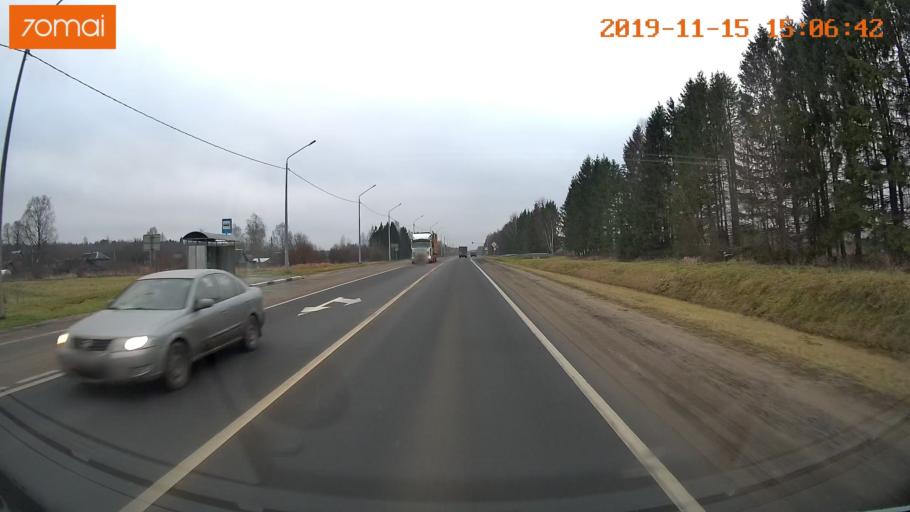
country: RU
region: Jaroslavl
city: Prechistoye
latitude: 58.3903
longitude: 40.3066
